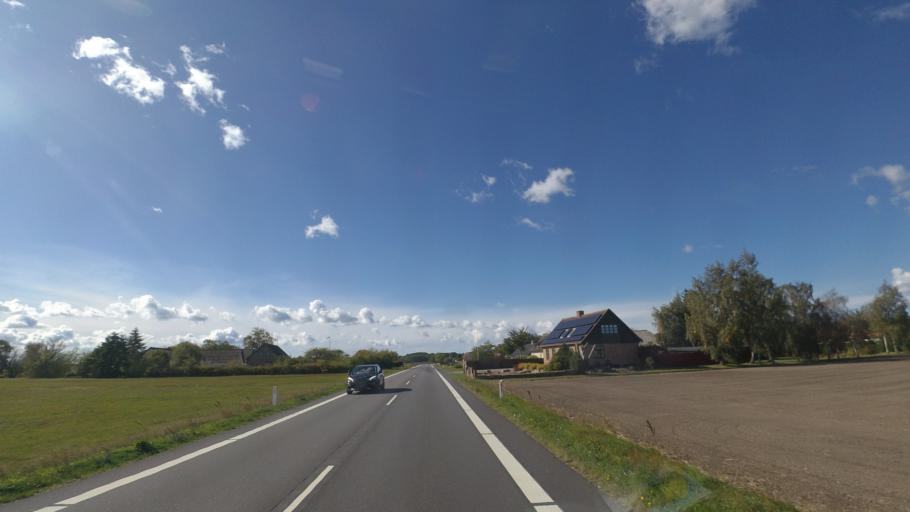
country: DK
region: Capital Region
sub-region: Bornholm Kommune
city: Nexo
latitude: 55.0607
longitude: 15.0528
